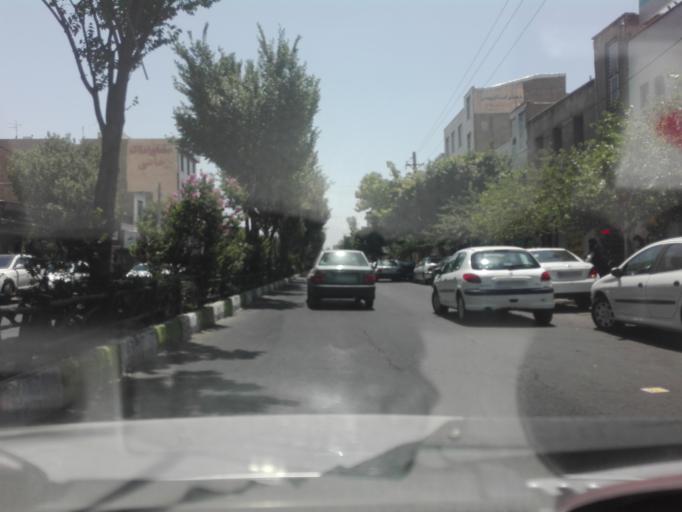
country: IR
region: Tehran
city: Shahre Jadide Andisheh
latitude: 35.7294
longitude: 50.9897
